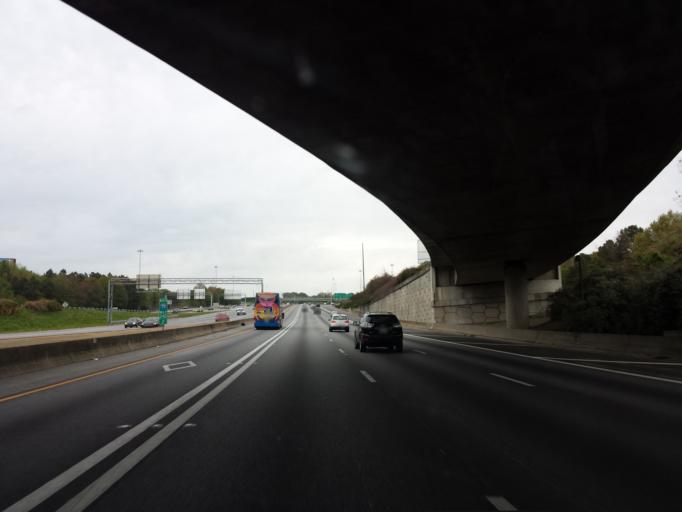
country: US
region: Georgia
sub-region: Fulton County
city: Hapeville
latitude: 33.6890
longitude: -84.4001
